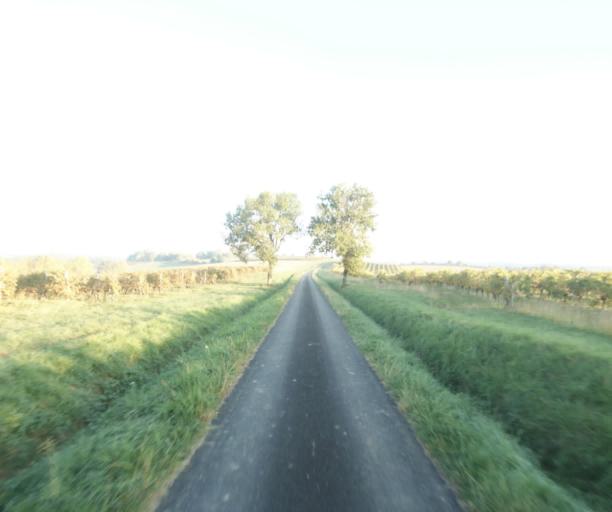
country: FR
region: Midi-Pyrenees
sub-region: Departement du Gers
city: Gondrin
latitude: 43.7769
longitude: 0.1869
